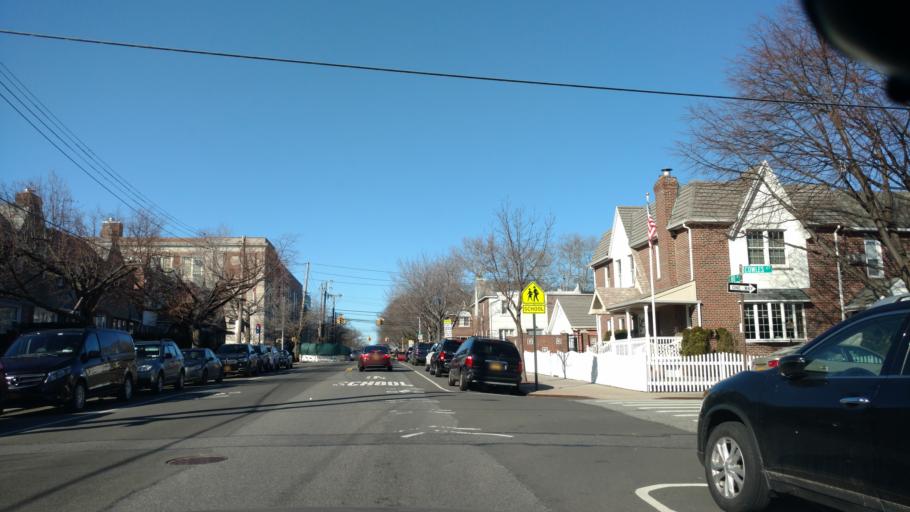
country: US
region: New York
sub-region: Kings County
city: East New York
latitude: 40.7187
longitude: -73.8741
